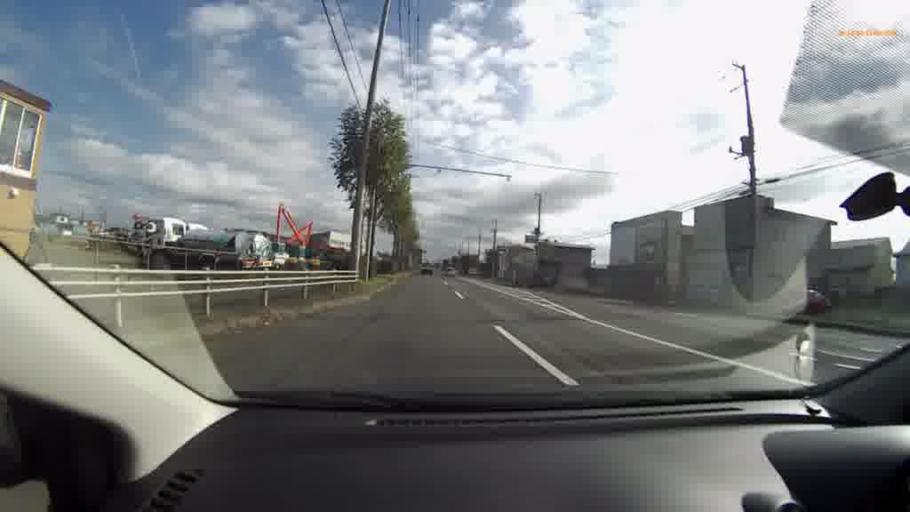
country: JP
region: Hokkaido
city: Kushiro
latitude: 43.0109
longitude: 144.2940
